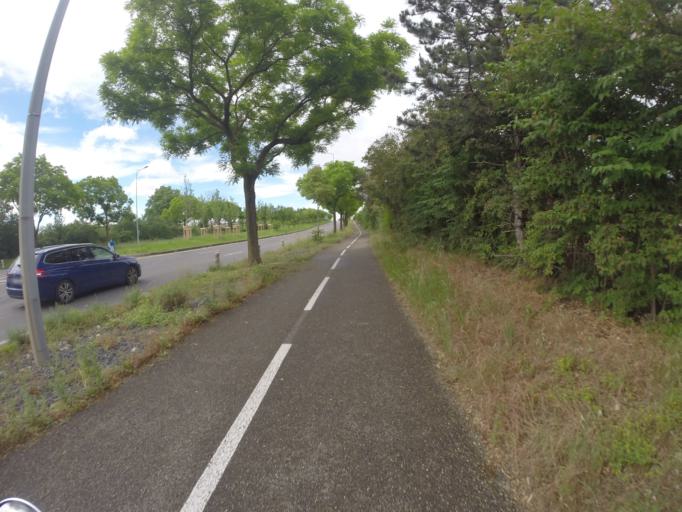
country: FR
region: Rhone-Alpes
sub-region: Departement du Rhone
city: Bron
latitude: 45.7302
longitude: 4.9295
